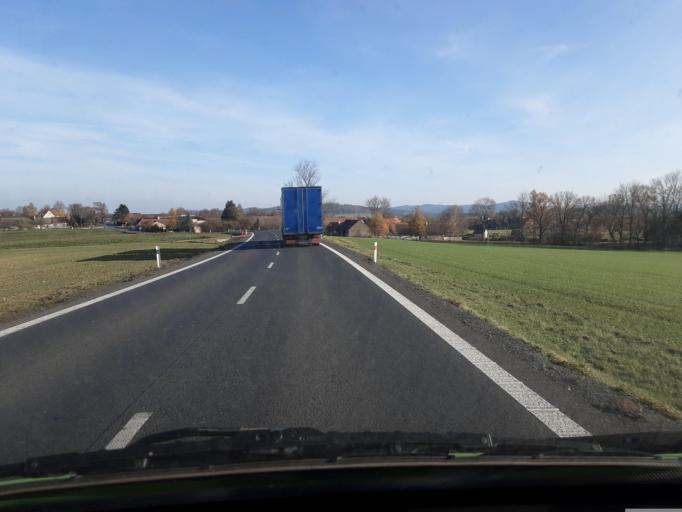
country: CZ
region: Plzensky
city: Horazd'ovice
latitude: 49.3254
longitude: 13.5900
